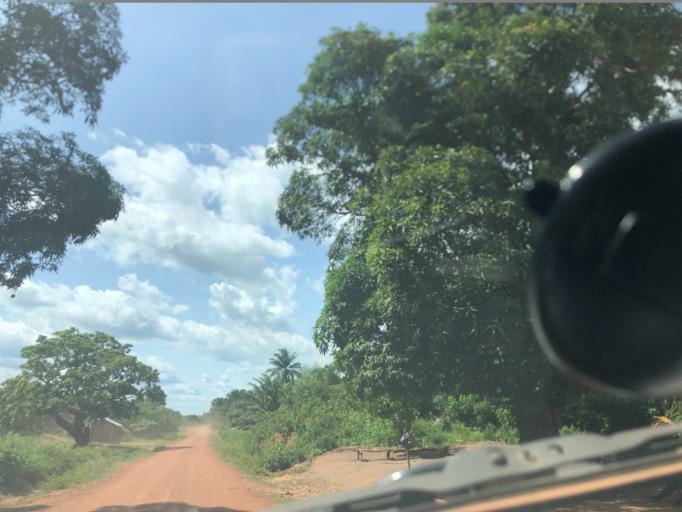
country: CD
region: Equateur
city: Libenge
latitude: 3.9317
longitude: 18.6980
